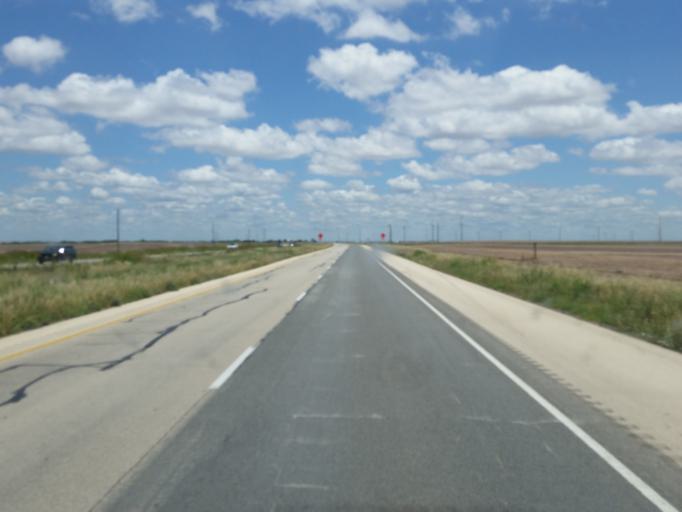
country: US
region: Texas
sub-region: Nolan County
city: Roscoe
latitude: 32.4777
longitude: -100.6146
